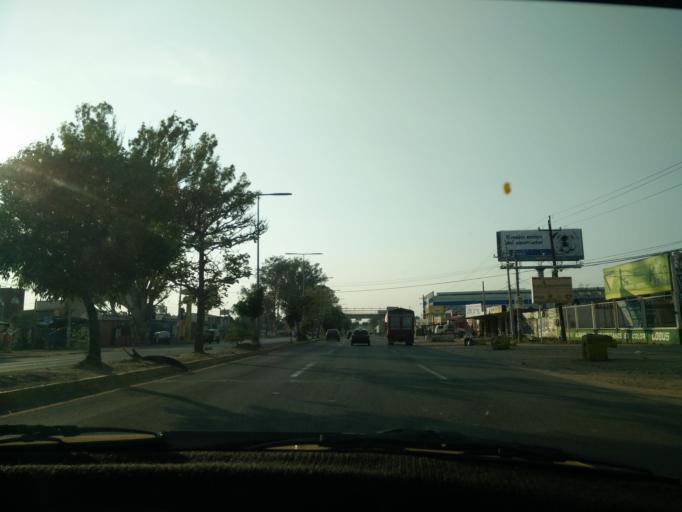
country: MX
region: Oaxaca
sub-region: Santa Maria Atzompa
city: Fraccionamiento Riberas de San Jeronimo
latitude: 17.1274
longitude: -96.7682
